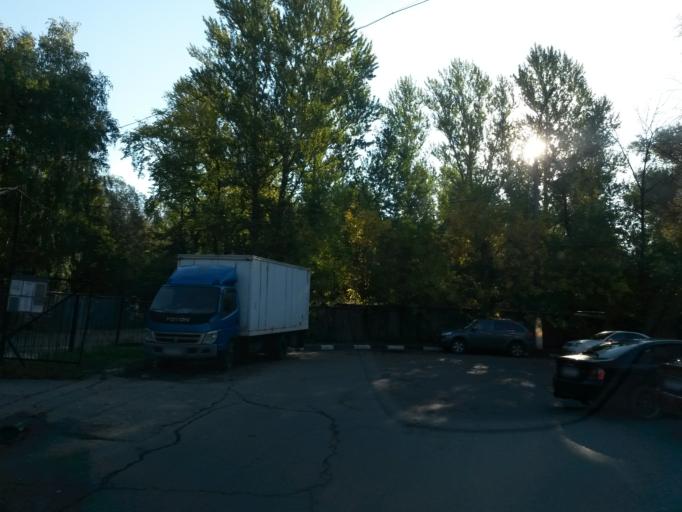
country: RU
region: Moscow
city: Kapotnya
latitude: 55.6403
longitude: 37.7996
